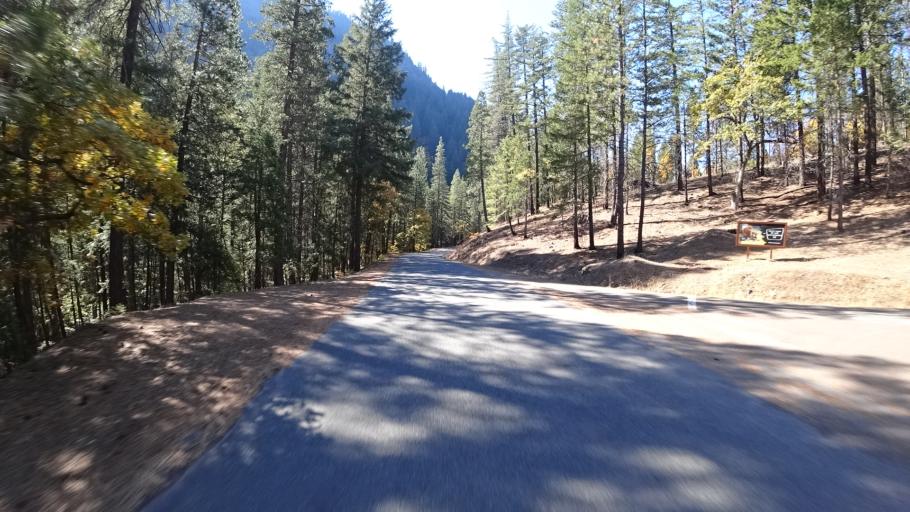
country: US
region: California
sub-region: Siskiyou County
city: Happy Camp
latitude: 41.6400
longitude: -123.0531
